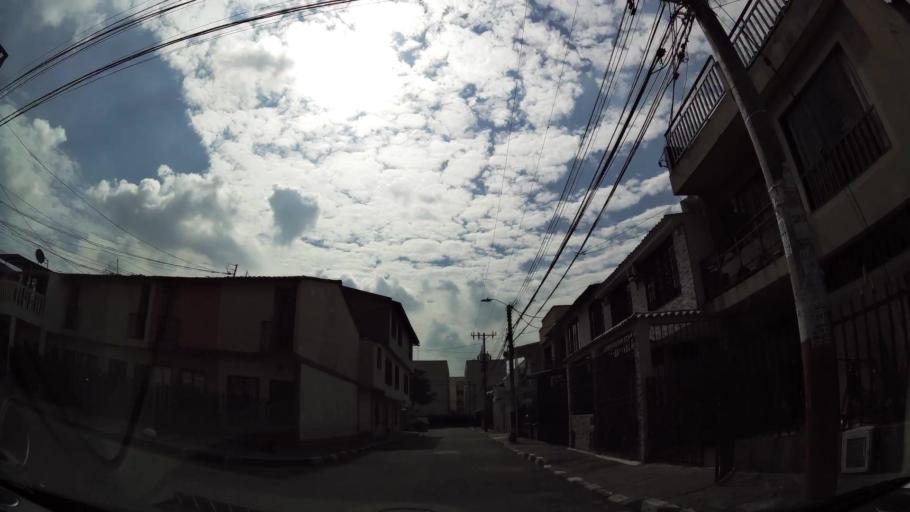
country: CO
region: Valle del Cauca
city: Cali
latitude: 3.4943
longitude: -76.4983
